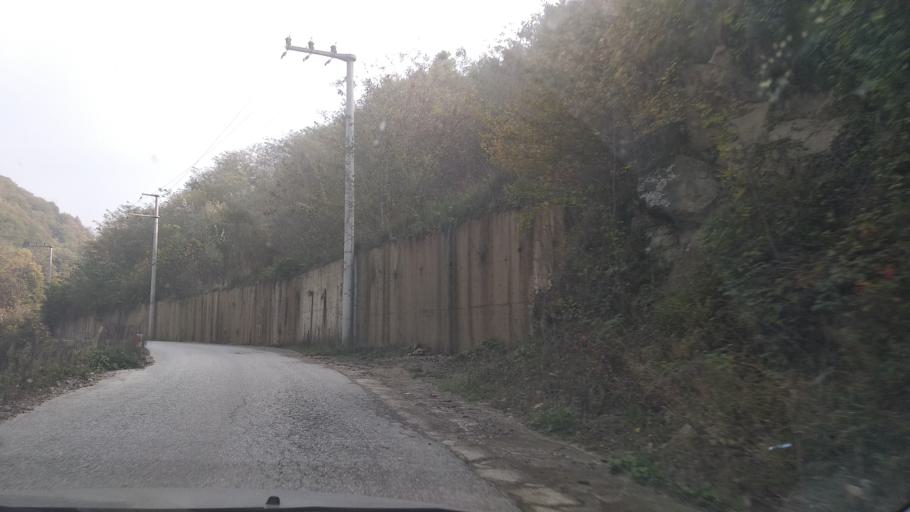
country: TR
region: Duzce
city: Kaynasli
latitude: 40.7314
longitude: 31.2278
